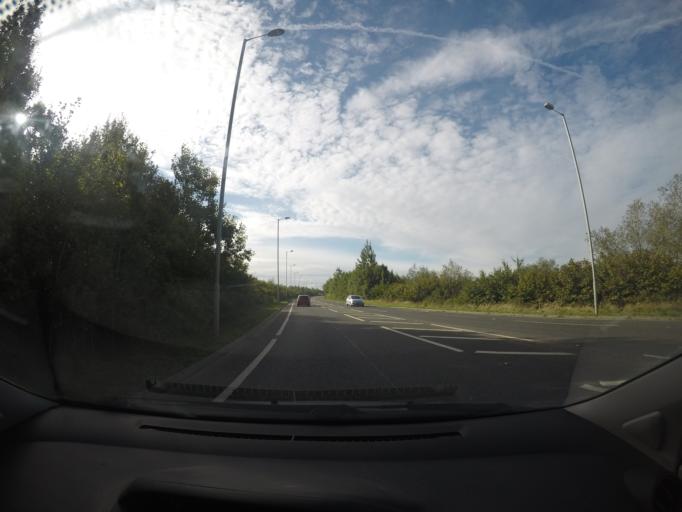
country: GB
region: England
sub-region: North Yorkshire
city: Barlby
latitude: 53.7819
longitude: -1.0359
